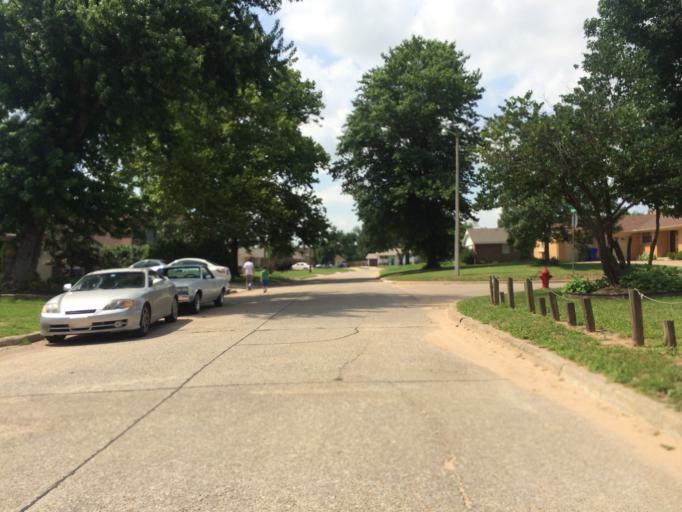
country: US
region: Oklahoma
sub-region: Cleveland County
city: Norman
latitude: 35.2129
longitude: -97.4831
